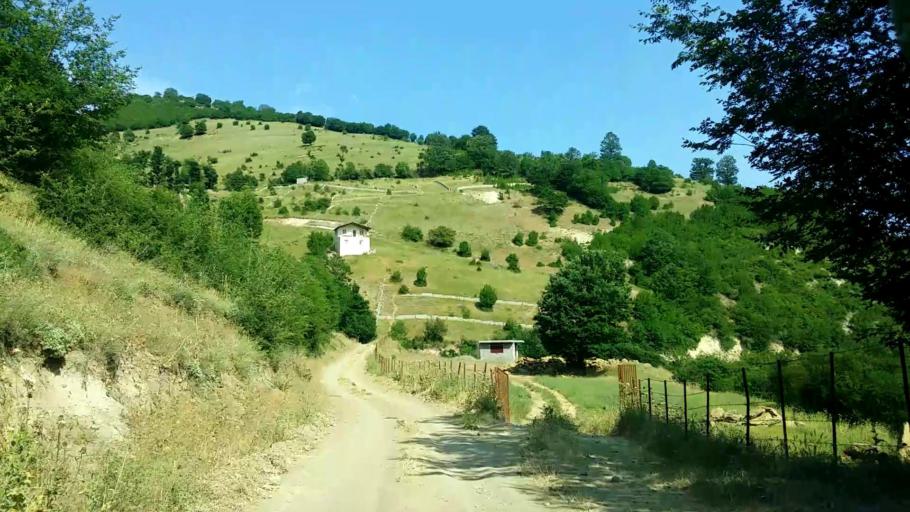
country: IR
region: Mazandaran
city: Chalus
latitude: 36.5544
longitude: 51.2934
